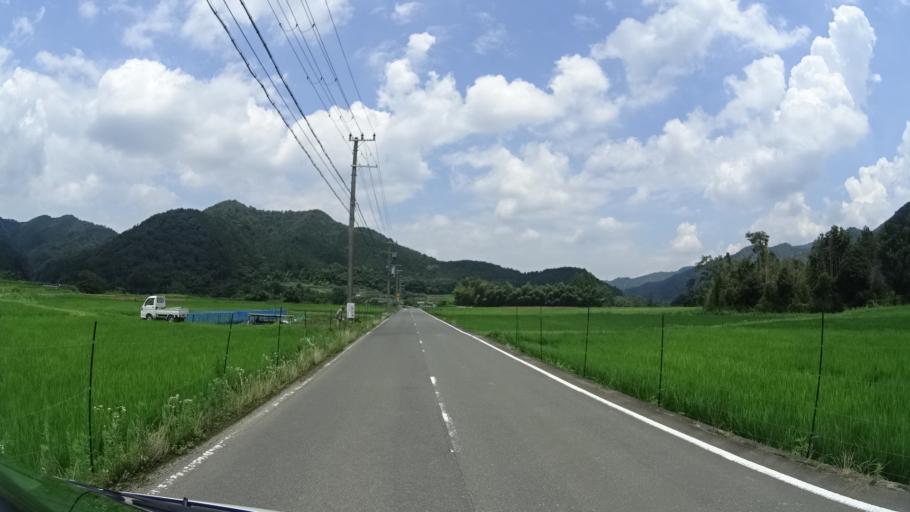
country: JP
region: Kyoto
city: Ayabe
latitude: 35.1997
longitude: 135.2446
